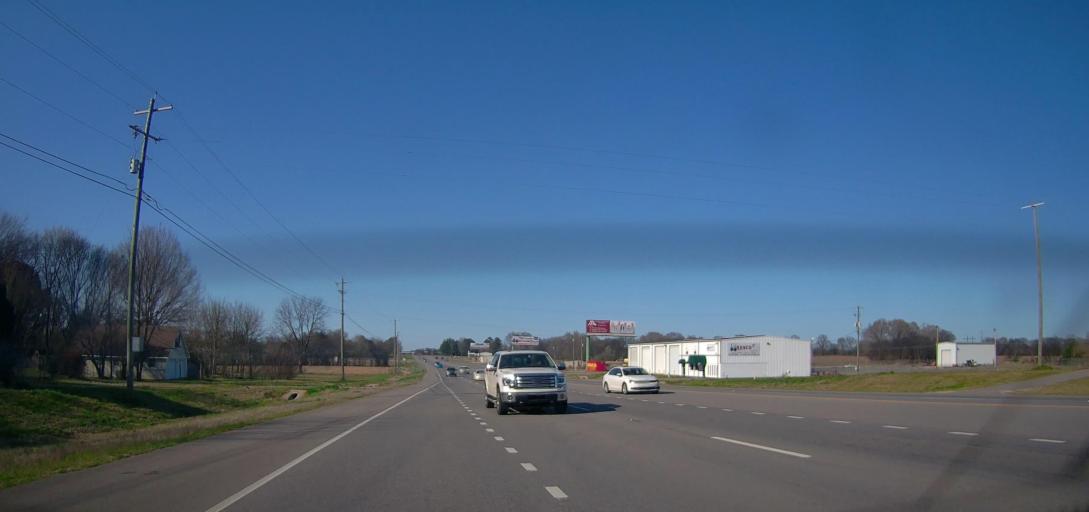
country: US
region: Alabama
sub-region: Colbert County
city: Muscle Shoals
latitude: 34.7018
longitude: -87.6351
